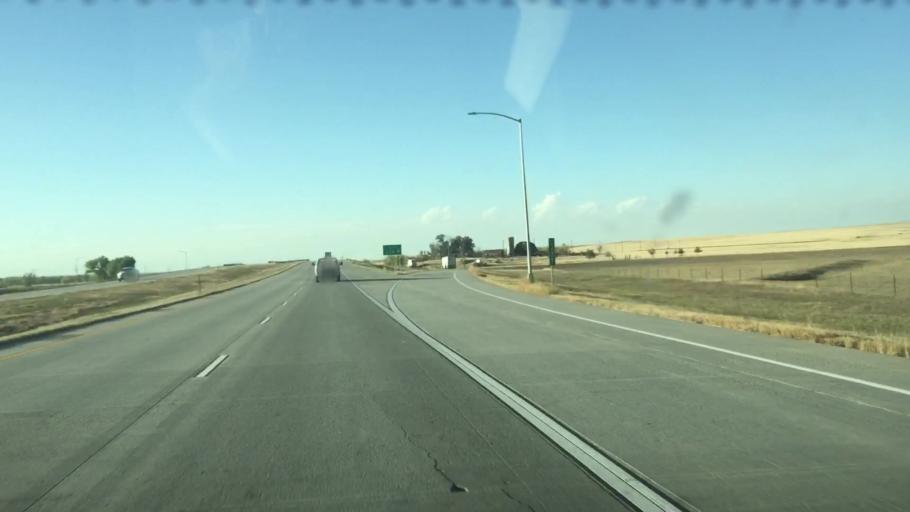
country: US
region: Colorado
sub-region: Arapahoe County
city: Byers
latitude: 39.5026
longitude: -103.9697
